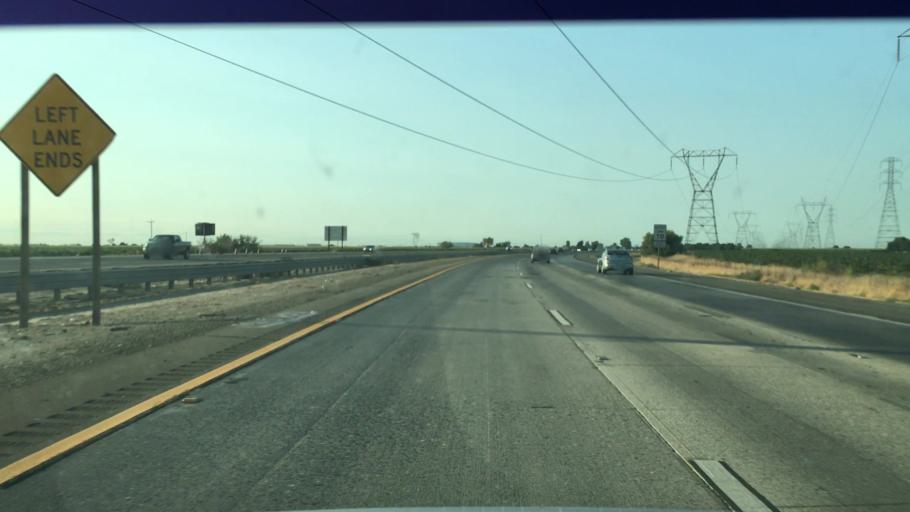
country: US
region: California
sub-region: San Joaquin County
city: Woodbridge
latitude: 38.1227
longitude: -121.4003
